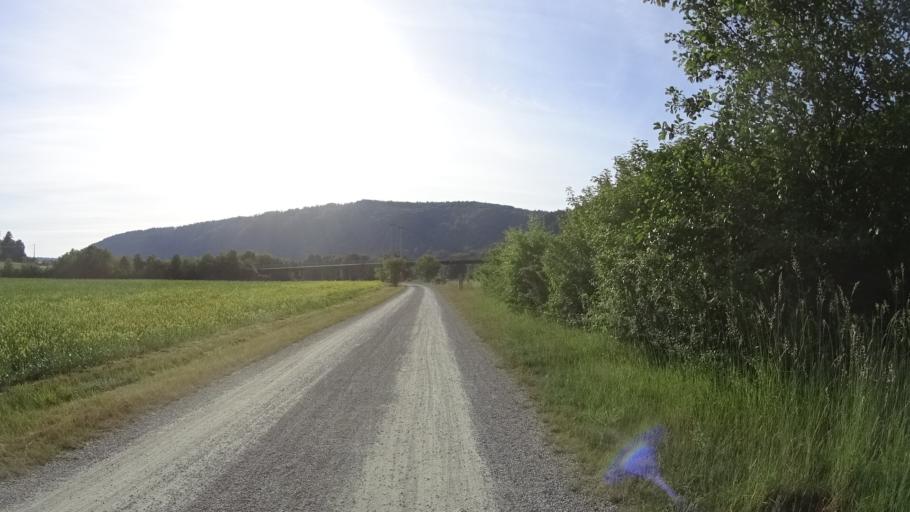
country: DE
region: Bavaria
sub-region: Lower Bavaria
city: Riedenburg
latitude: 48.9757
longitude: 11.6521
